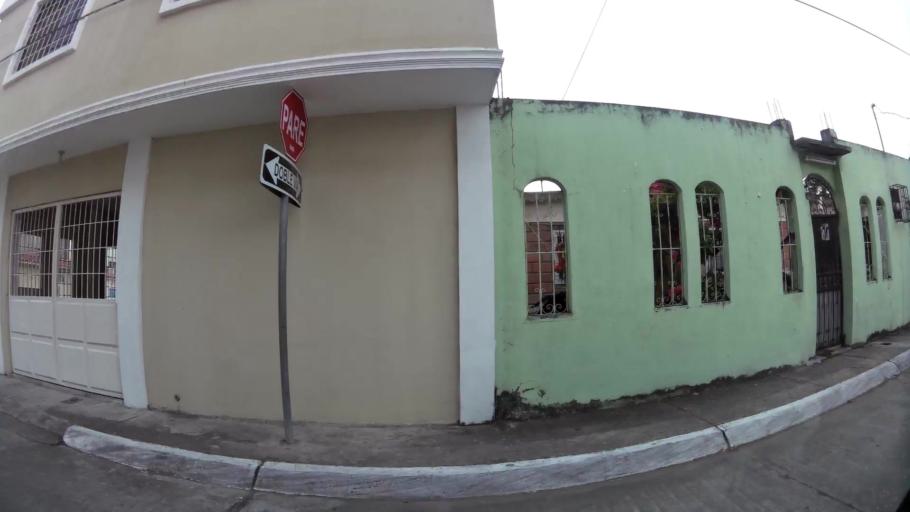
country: EC
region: Guayas
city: Eloy Alfaro
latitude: -2.1202
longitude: -79.8860
